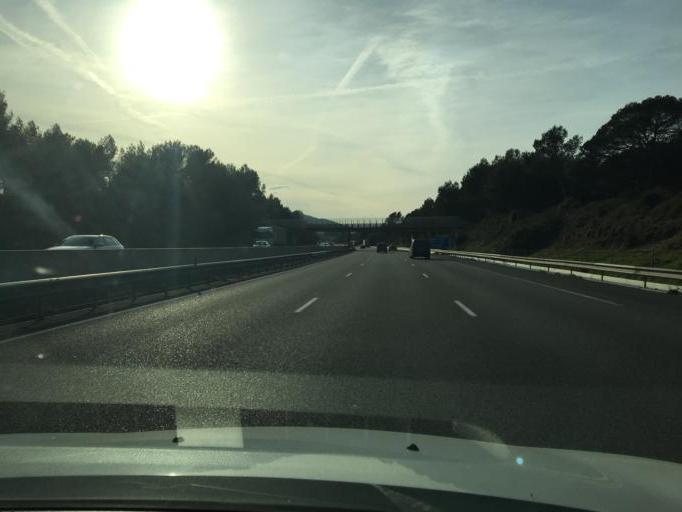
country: FR
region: Provence-Alpes-Cote d'Azur
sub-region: Departement du Var
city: Puget-sur-Argens
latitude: 43.4673
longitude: 6.6595
